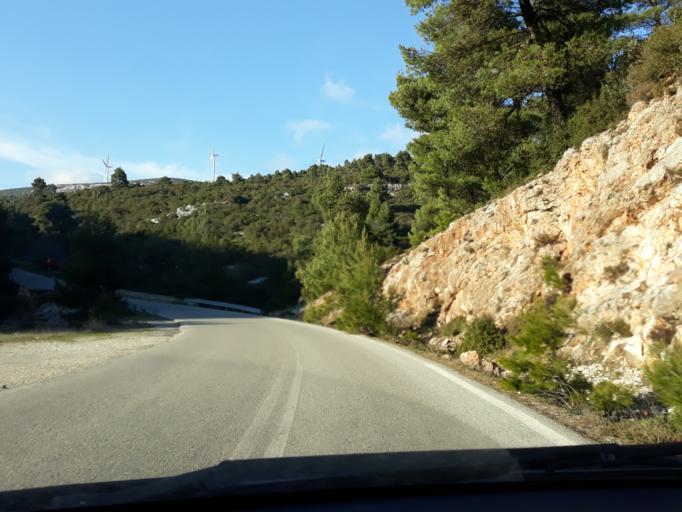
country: GR
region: Attica
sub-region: Nomarchia Dytikis Attikis
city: Fyli
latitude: 38.1561
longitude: 23.6309
